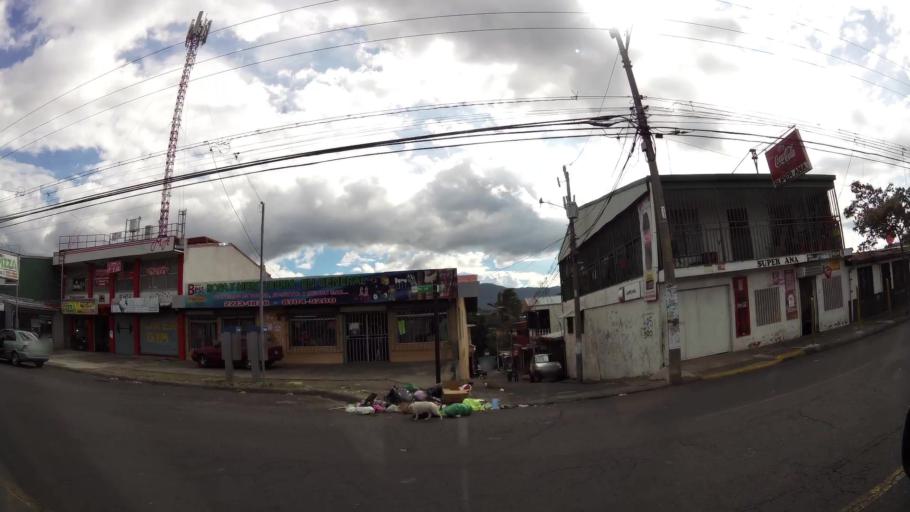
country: CR
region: Heredia
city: La Asuncion
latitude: 9.9573
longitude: -84.1582
